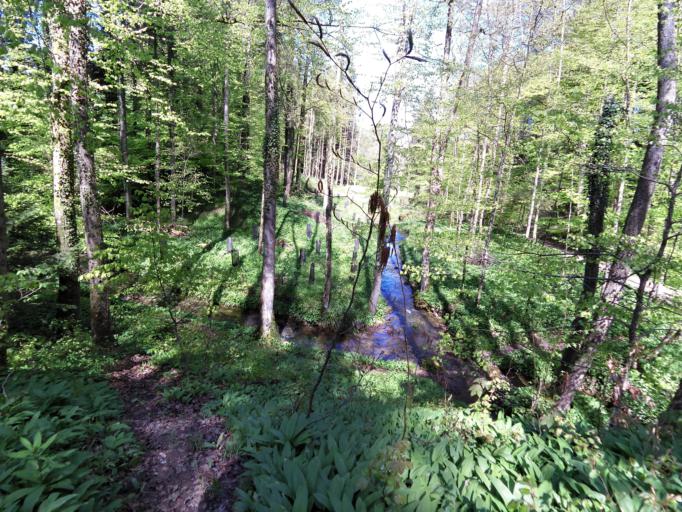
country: CH
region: Thurgau
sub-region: Weinfelden District
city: Maerstetten-Dorf
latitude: 47.6031
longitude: 9.1016
